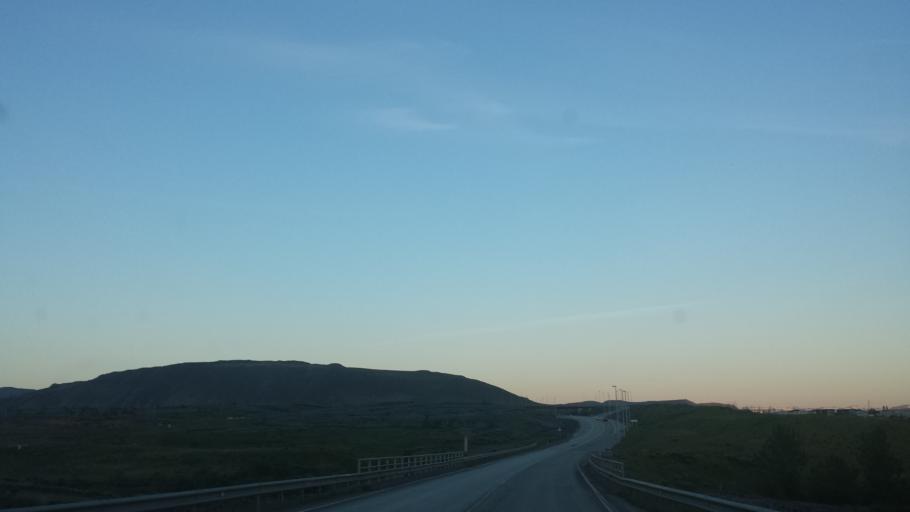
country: IS
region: Capital Region
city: Mosfellsbaer
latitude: 64.1890
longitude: -21.6866
